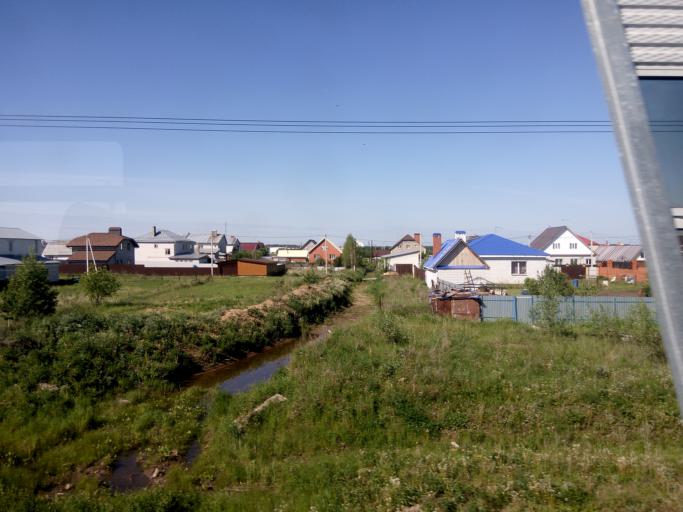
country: RU
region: Tatarstan
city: Stolbishchi
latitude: 55.6611
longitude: 49.2229
